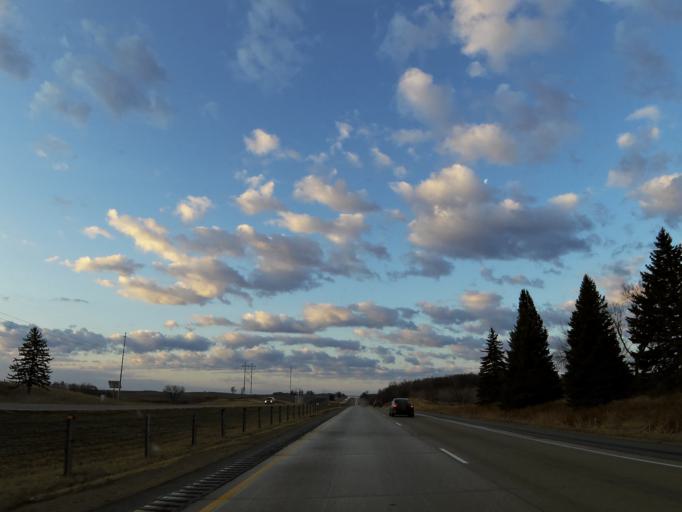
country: US
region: Minnesota
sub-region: Rice County
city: Dundas
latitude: 44.4148
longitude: -93.2925
